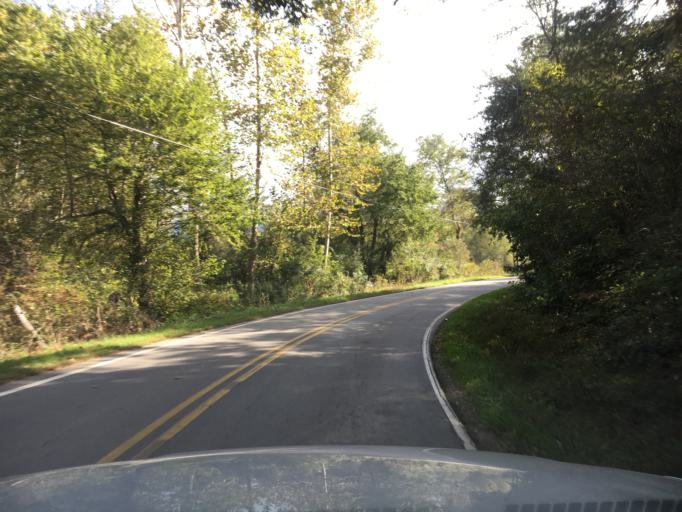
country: US
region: North Carolina
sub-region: Buncombe County
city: Swannanoa
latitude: 35.6045
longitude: -82.4323
